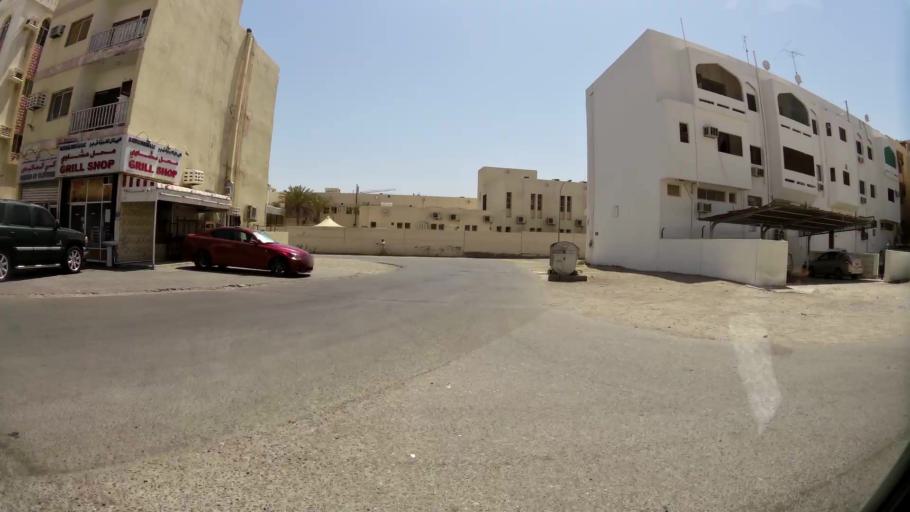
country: OM
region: Muhafazat Masqat
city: Muscat
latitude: 23.5978
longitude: 58.5431
